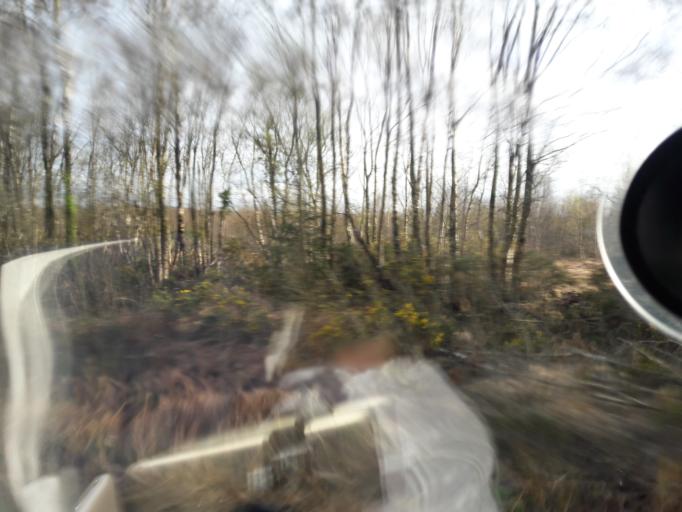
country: IE
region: Leinster
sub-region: An Iarmhi
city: Kinnegad
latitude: 53.4764
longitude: -7.0436
